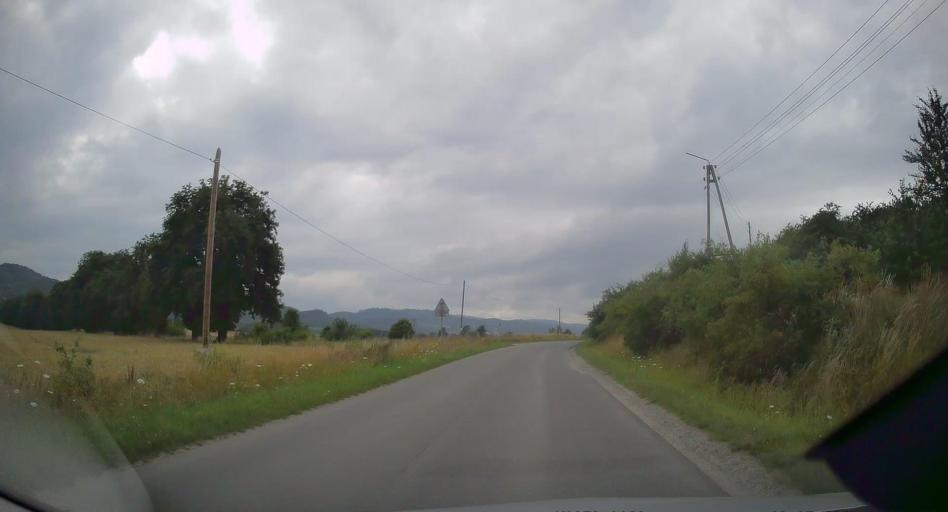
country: PL
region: Lower Silesian Voivodeship
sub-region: Powiat zabkowicki
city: Budzow
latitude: 50.5549
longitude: 16.7067
